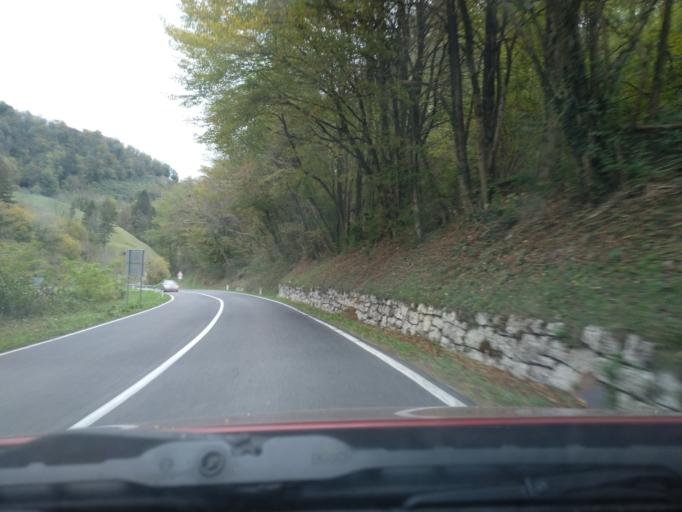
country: SI
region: Tolmin
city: Tolmin
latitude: 46.1467
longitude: 13.7154
